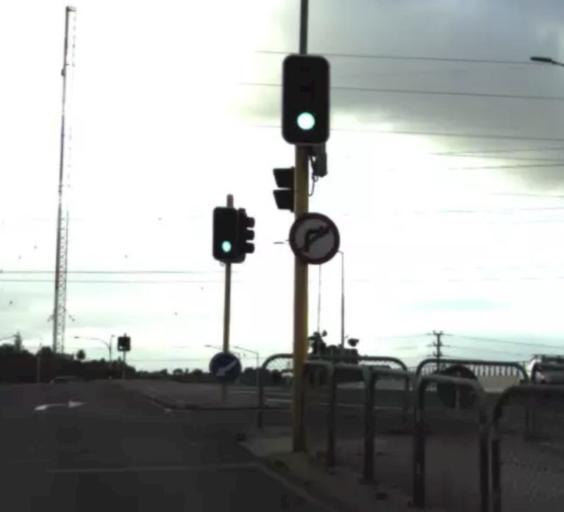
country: NZ
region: Auckland
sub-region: Auckland
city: Rosebank
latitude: -36.8490
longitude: 174.6317
